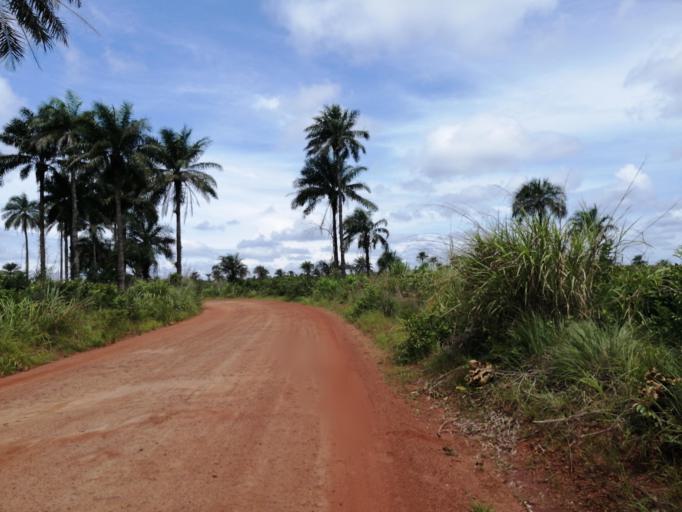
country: SL
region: Northern Province
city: Pepel
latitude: 8.6498
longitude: -13.0114
